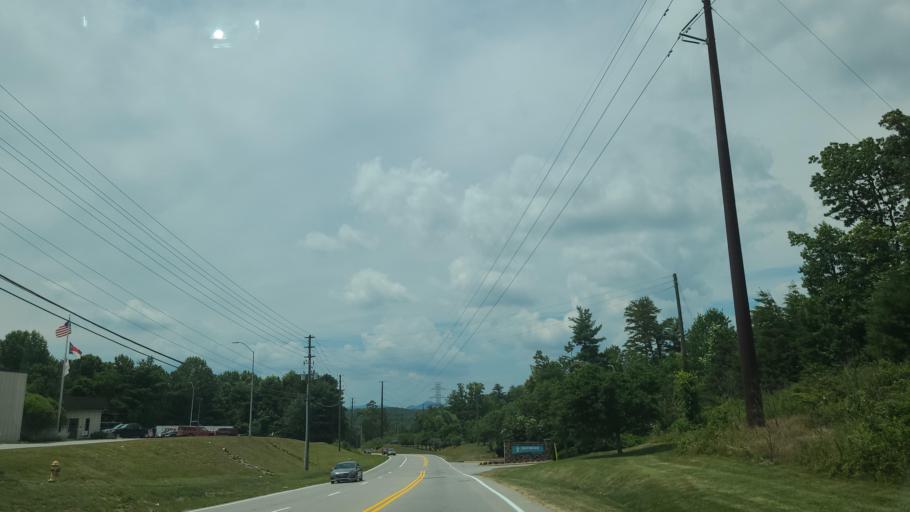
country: US
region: North Carolina
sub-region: Buncombe County
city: Avery Creek
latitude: 35.4812
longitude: -82.5666
